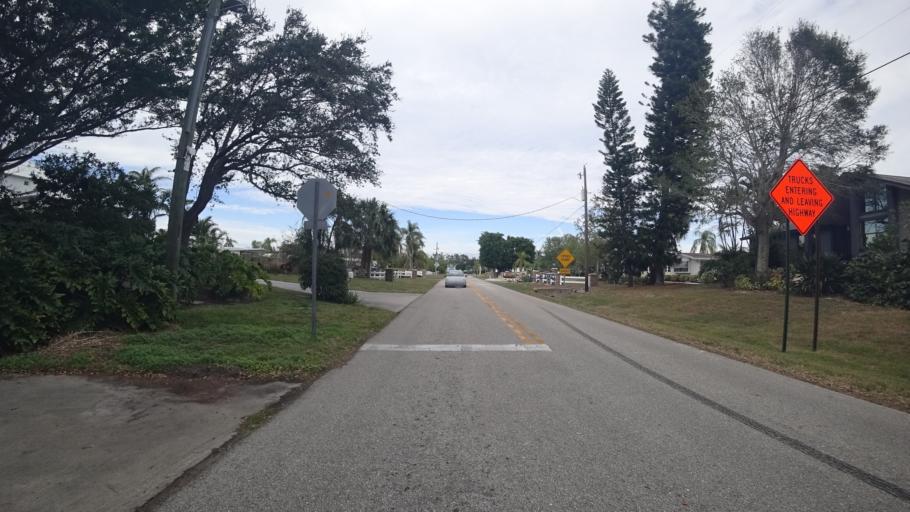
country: US
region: Florida
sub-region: Manatee County
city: West Bradenton
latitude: 27.4805
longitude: -82.6431
